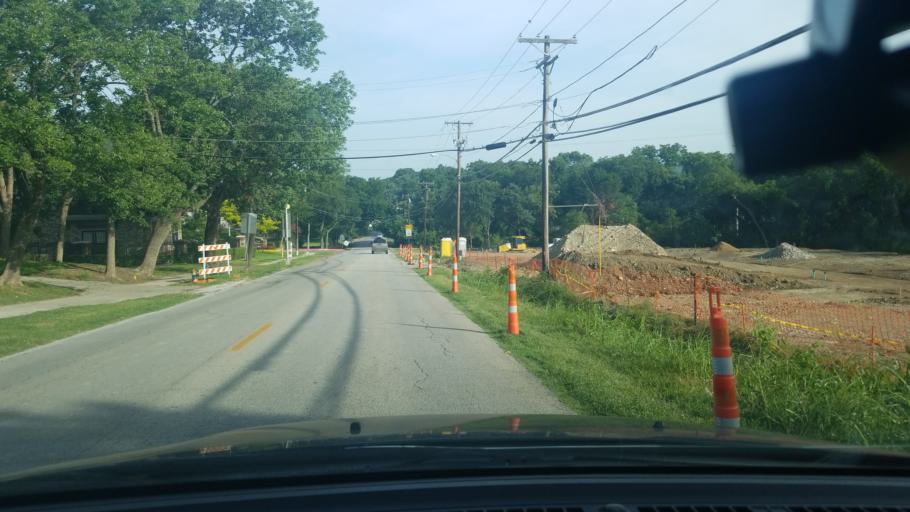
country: US
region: Texas
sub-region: Dallas County
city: Highland Park
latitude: 32.8034
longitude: -96.7158
